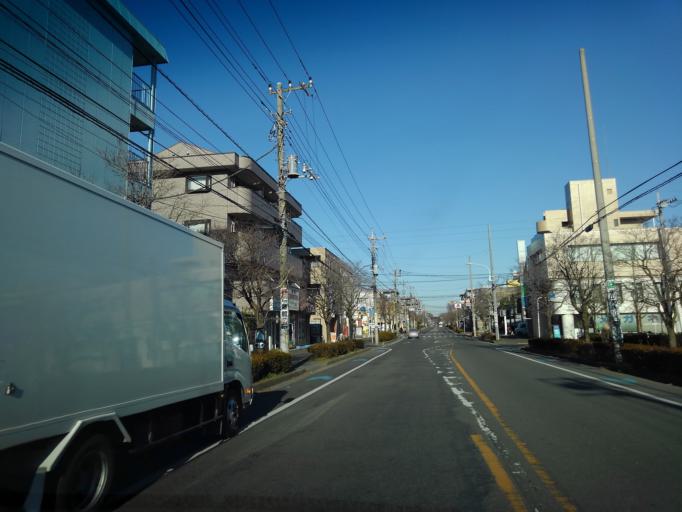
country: JP
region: Saitama
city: Tokorozawa
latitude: 35.7962
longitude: 139.5124
